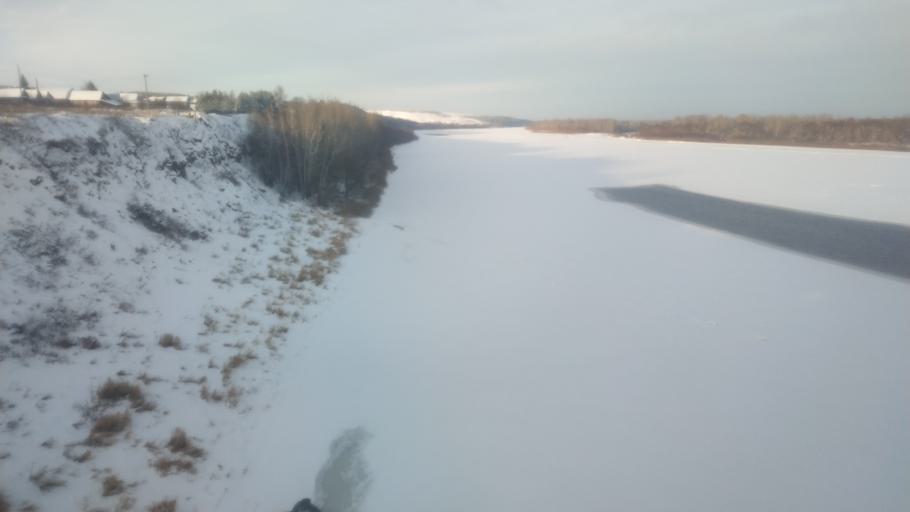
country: RU
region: Kirov
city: Vyatskiye Polyany
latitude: 56.2532
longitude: 51.0658
